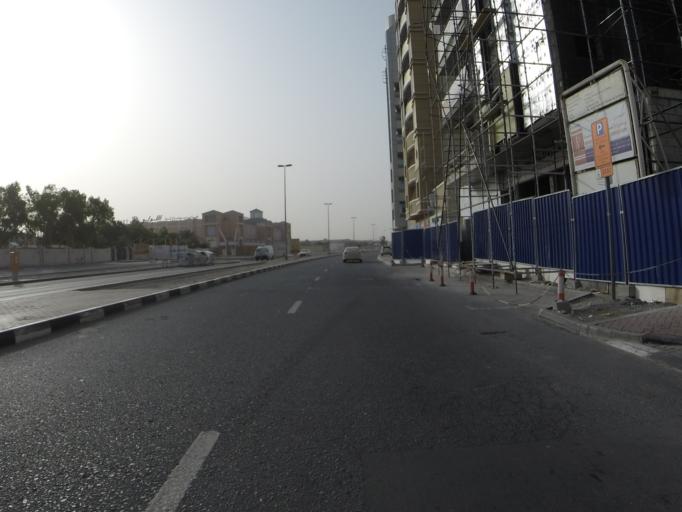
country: AE
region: Dubai
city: Dubai
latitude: 25.1178
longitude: 55.2043
